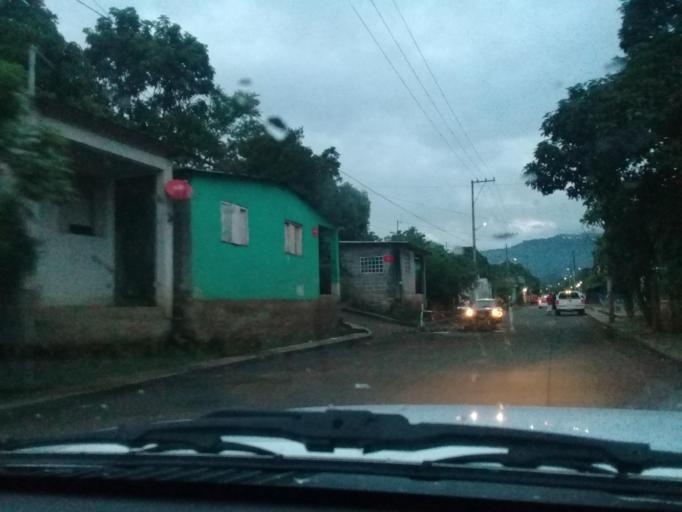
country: MX
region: Veracruz
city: San Andres Tuxtla
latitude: 18.4426
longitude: -95.2218
